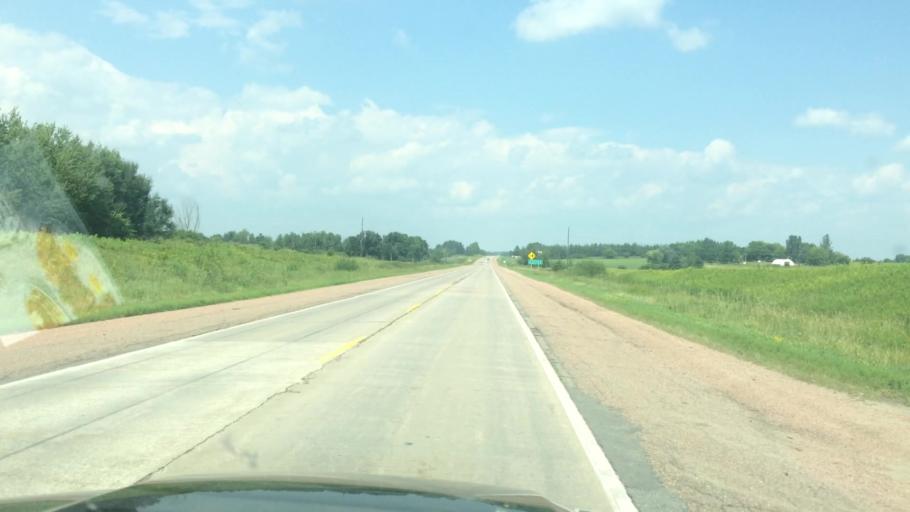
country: US
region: Wisconsin
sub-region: Clark County
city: Colby
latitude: 44.8703
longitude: -90.3157
